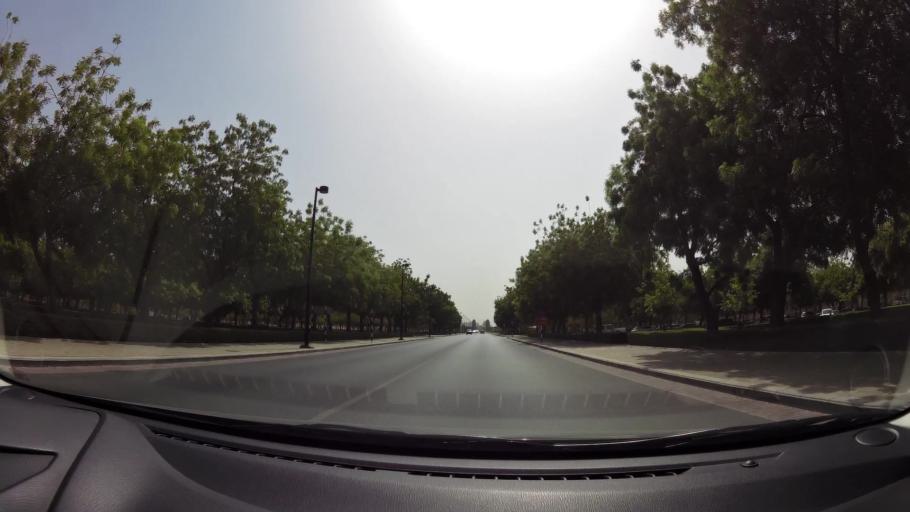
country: OM
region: Muhafazat Masqat
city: Bawshar
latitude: 23.5819
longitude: 58.3898
